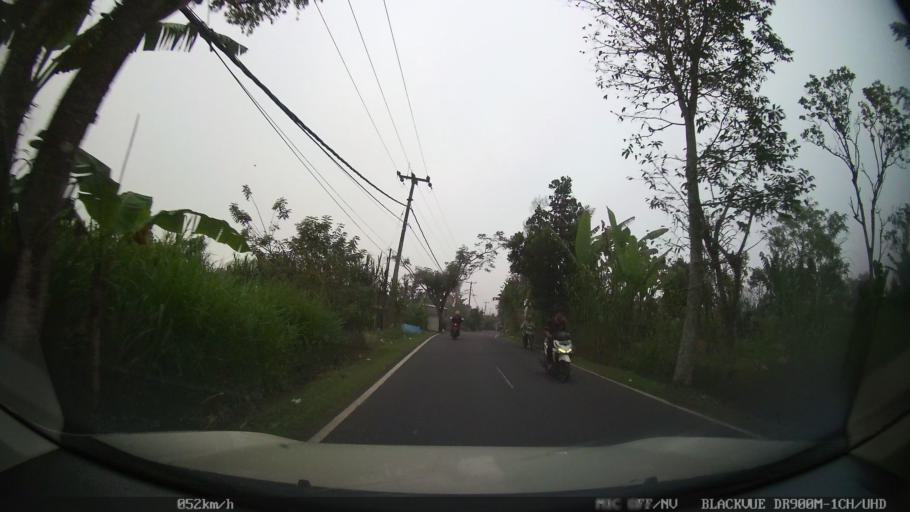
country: ID
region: Bali
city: Banjar Kedisan
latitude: -8.2934
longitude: 115.3155
